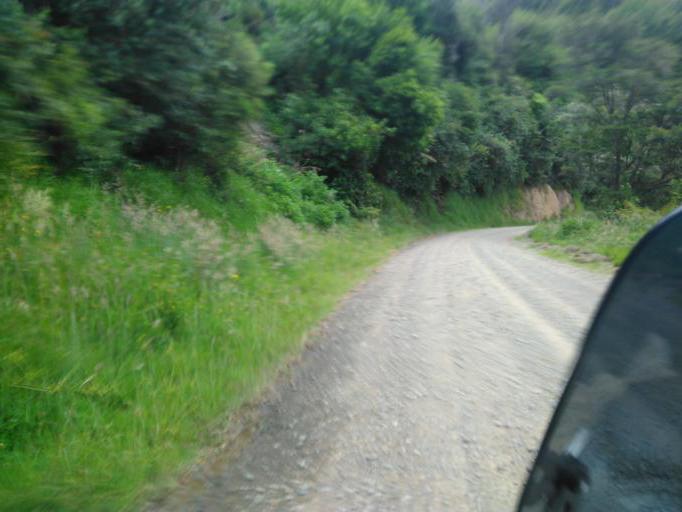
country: NZ
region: Bay of Plenty
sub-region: Opotiki District
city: Opotiki
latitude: -38.0334
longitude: 177.4421
